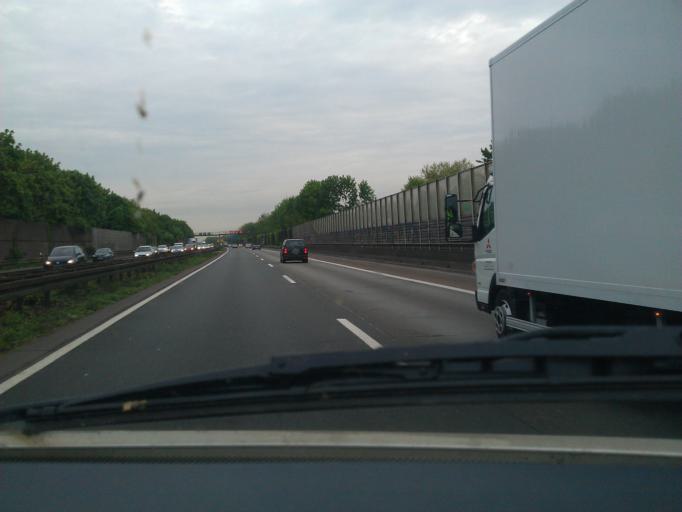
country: DE
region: North Rhine-Westphalia
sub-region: Regierungsbezirk Dusseldorf
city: Krefeld
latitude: 51.3592
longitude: 6.6269
